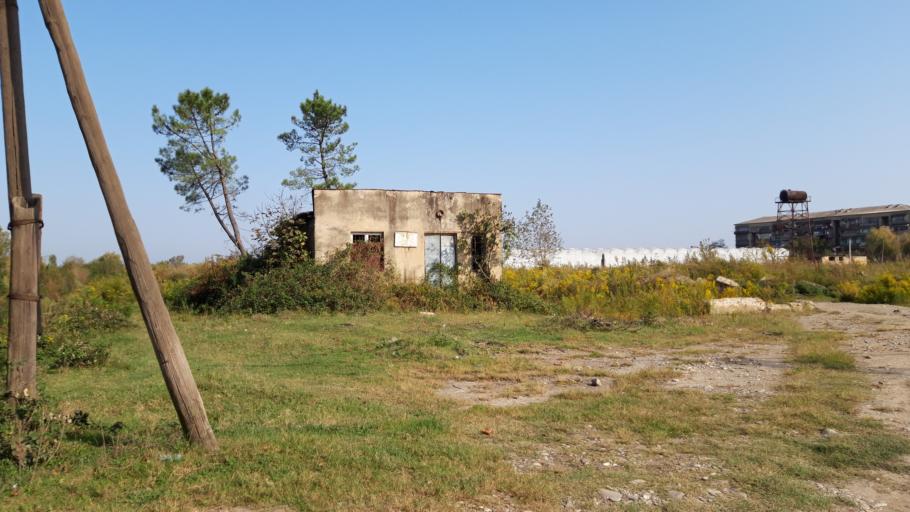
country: GE
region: Imereti
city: Samtredia
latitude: 42.1639
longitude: 42.3271
